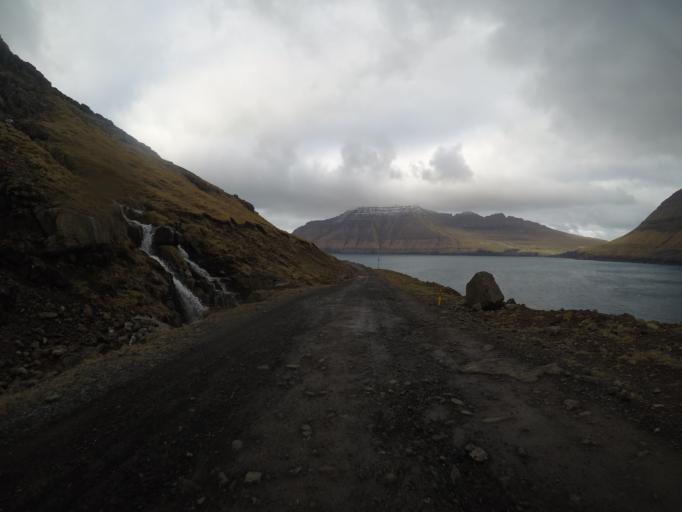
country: FO
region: Nordoyar
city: Klaksvik
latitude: 62.3420
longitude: -6.5807
